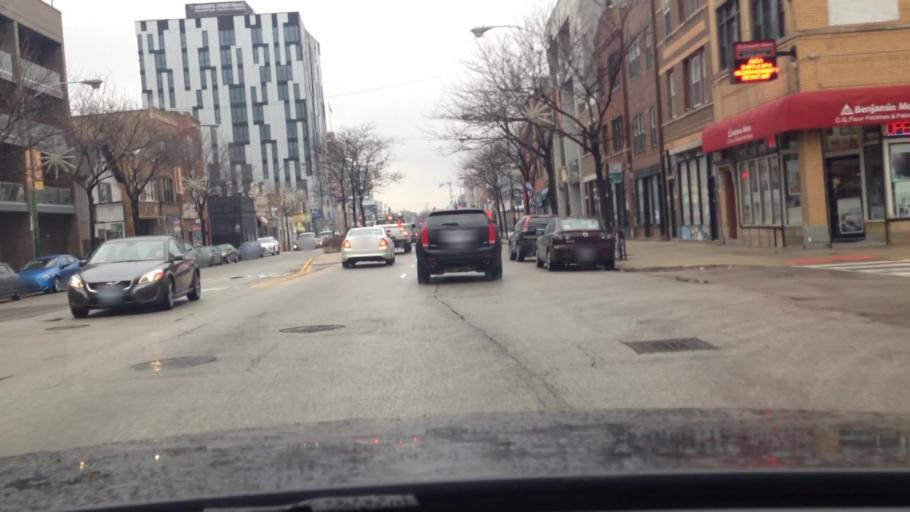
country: US
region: Illinois
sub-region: Cook County
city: Chicago
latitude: 41.9014
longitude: -87.6674
